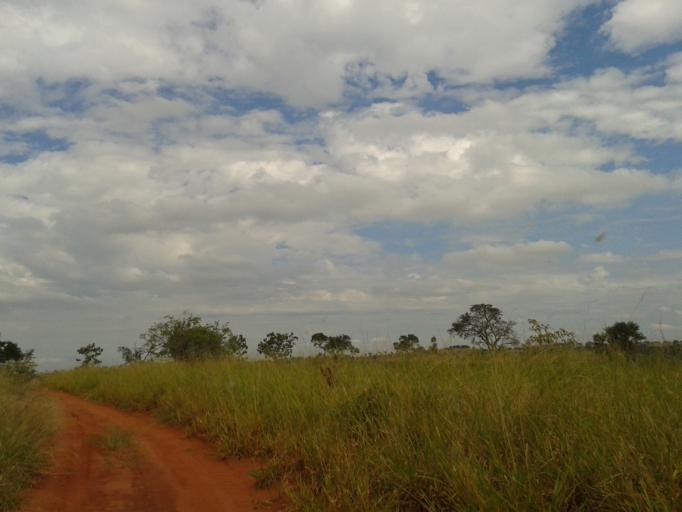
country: BR
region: Minas Gerais
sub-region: Campina Verde
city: Campina Verde
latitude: -19.3909
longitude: -49.6586
